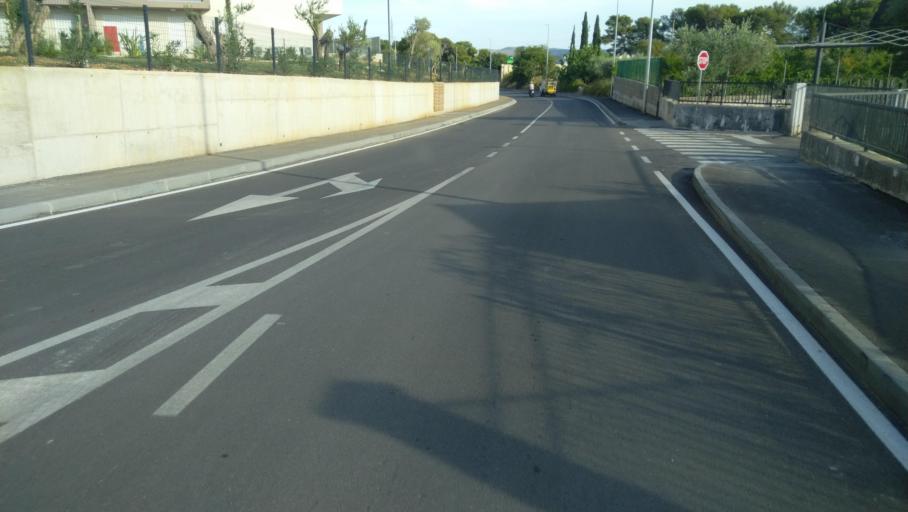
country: HR
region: Sibensko-Kniniska
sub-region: Grad Sibenik
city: Sibenik
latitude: 43.7195
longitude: 15.9120
